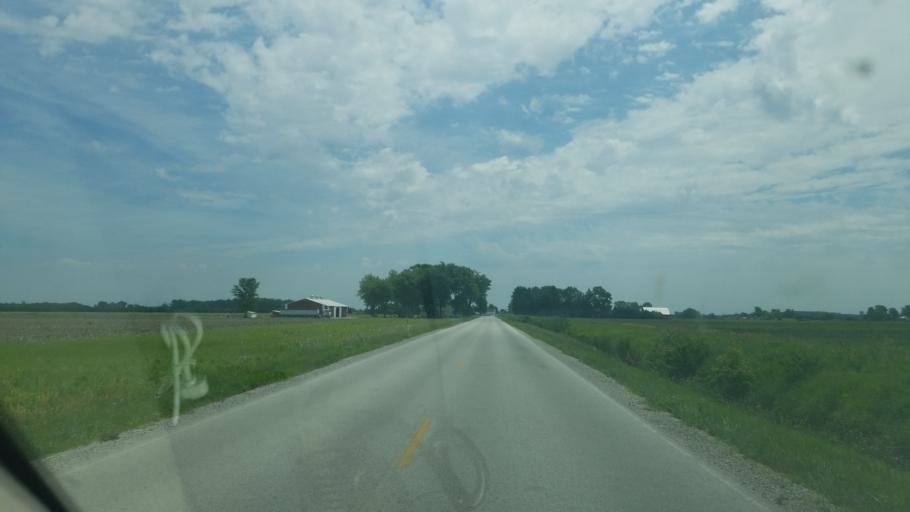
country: US
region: Ohio
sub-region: Wood County
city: Bowling Green
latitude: 41.2968
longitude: -83.6060
